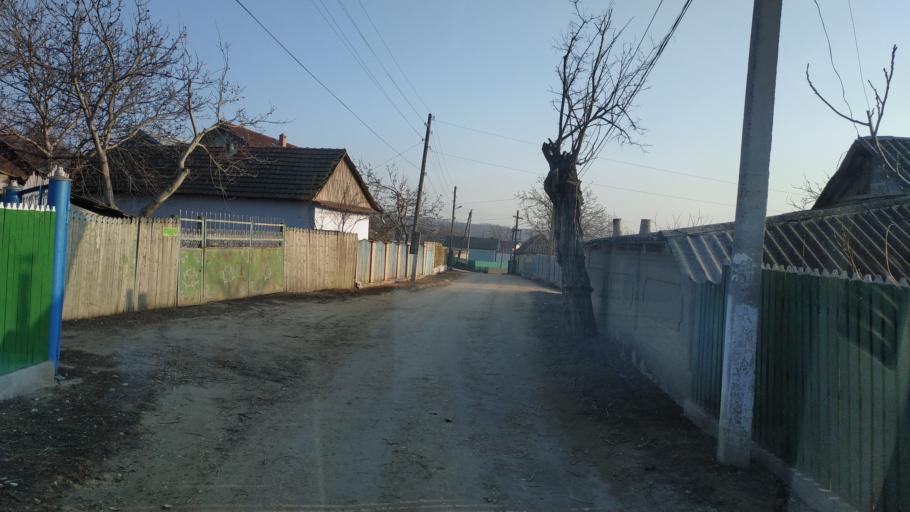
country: MD
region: Hincesti
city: Dancu
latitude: 46.7712
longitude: 28.3539
